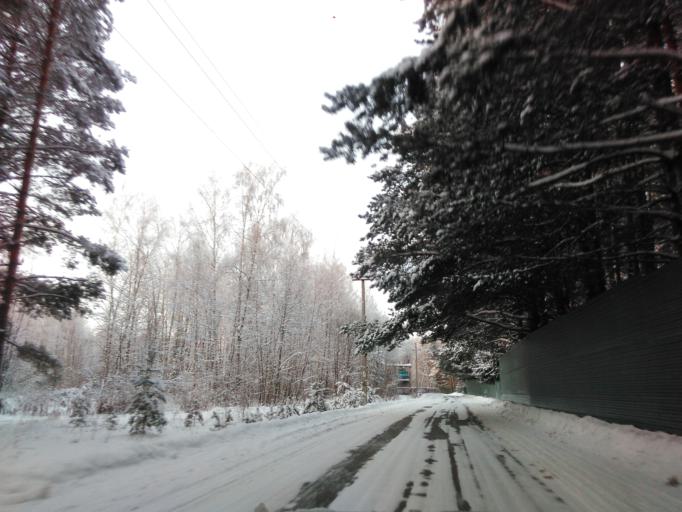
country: RU
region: Tverskaya
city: Konakovo
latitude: 56.6499
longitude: 36.6516
